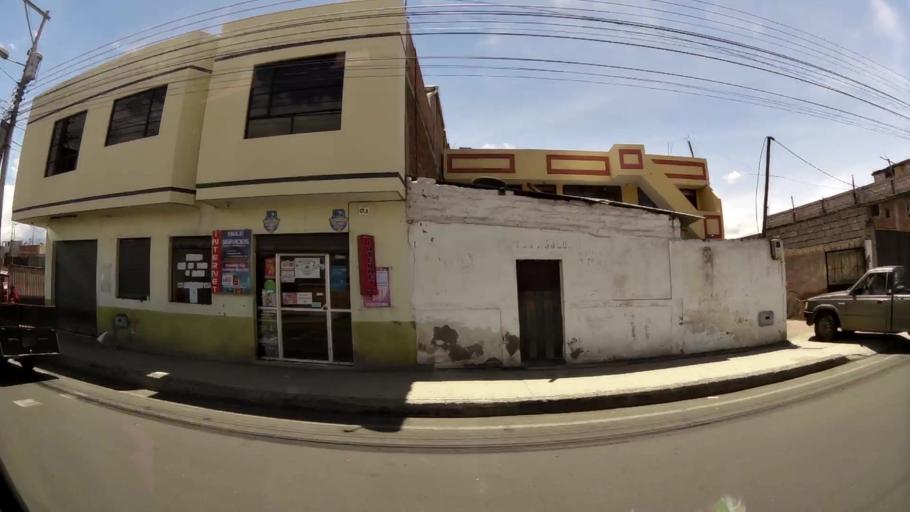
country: EC
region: Chimborazo
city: Riobamba
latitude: -1.6826
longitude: -78.6377
